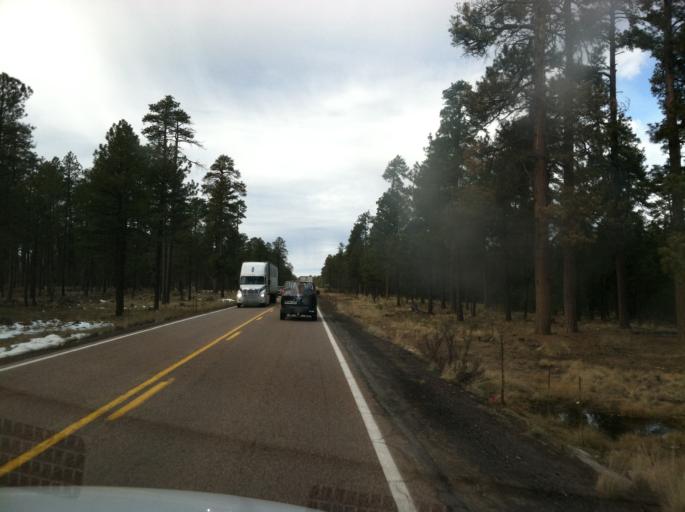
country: US
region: Arizona
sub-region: Navajo County
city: Heber-Overgaard
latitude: 34.2995
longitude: -110.8723
